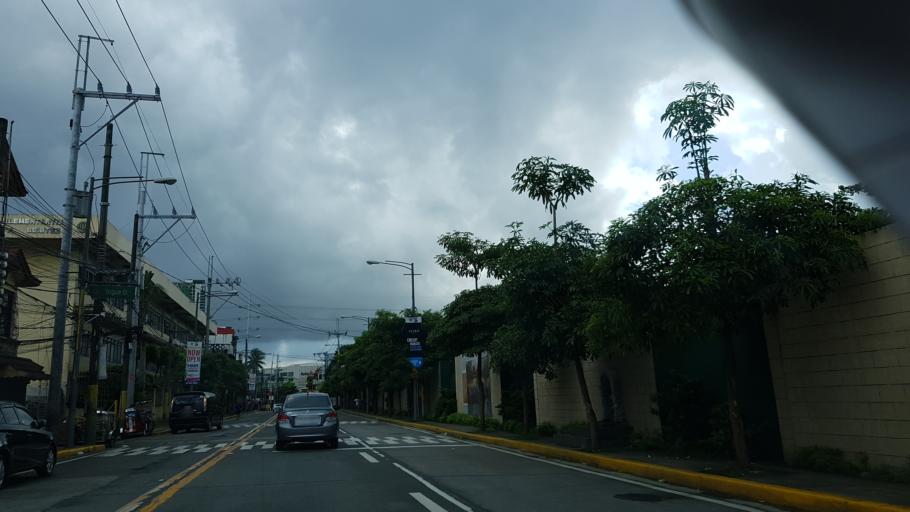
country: PH
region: Metro Manila
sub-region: Makati City
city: Makati City
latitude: 14.5672
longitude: 121.0175
